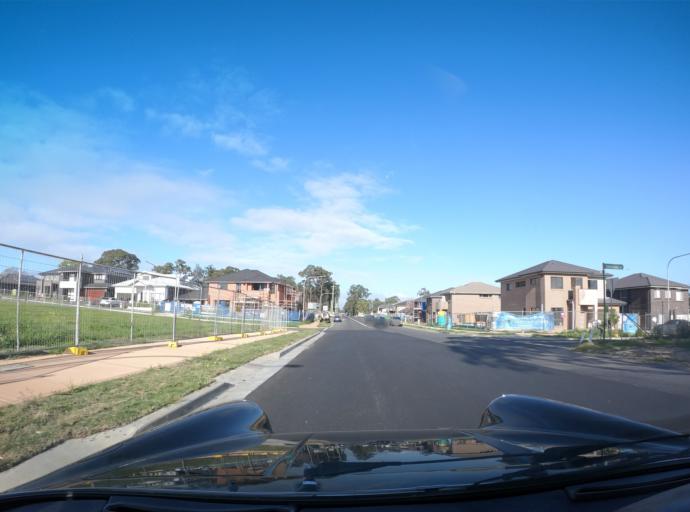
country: AU
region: New South Wales
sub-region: The Hills Shire
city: Beaumont Hills
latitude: -33.6841
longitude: 150.9563
